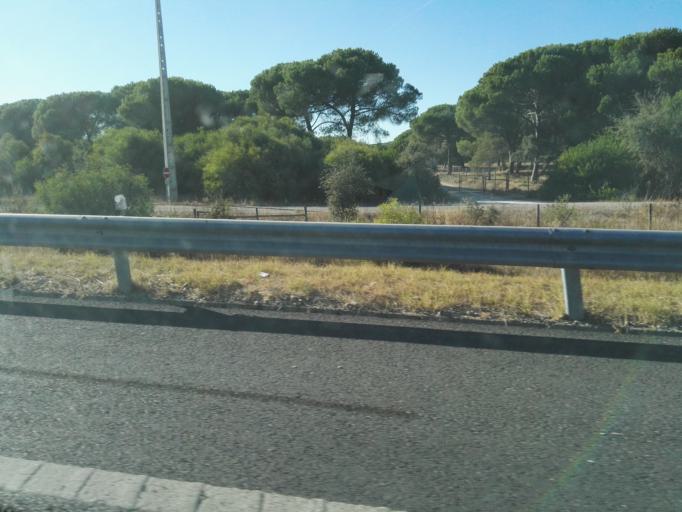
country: PT
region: Santarem
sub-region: Benavente
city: Benavente
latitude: 38.9574
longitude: -8.8256
